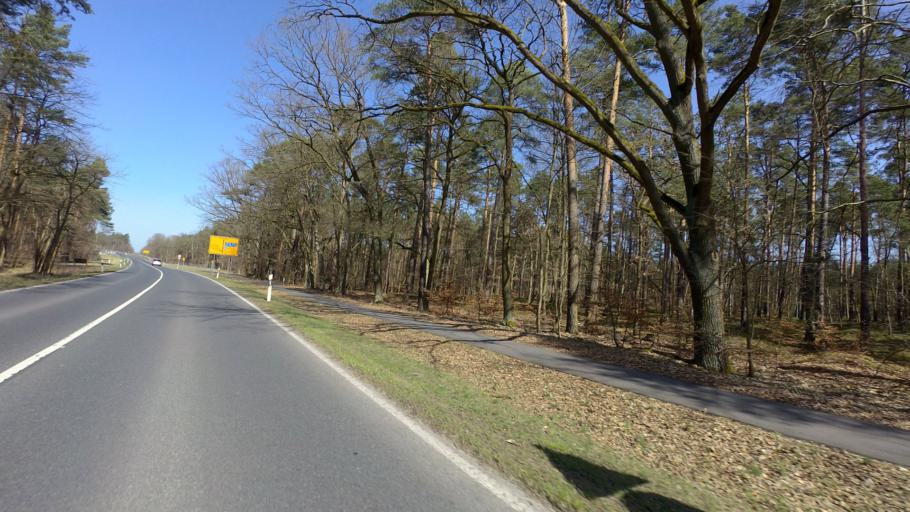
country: DE
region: Brandenburg
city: Oranienburg
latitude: 52.7882
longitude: 13.2375
